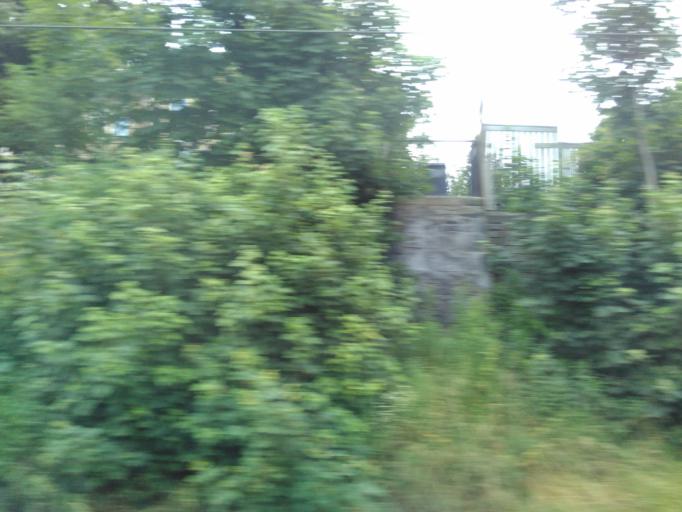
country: GB
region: Scotland
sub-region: Edinburgh
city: Colinton
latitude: 55.9321
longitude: -3.2339
